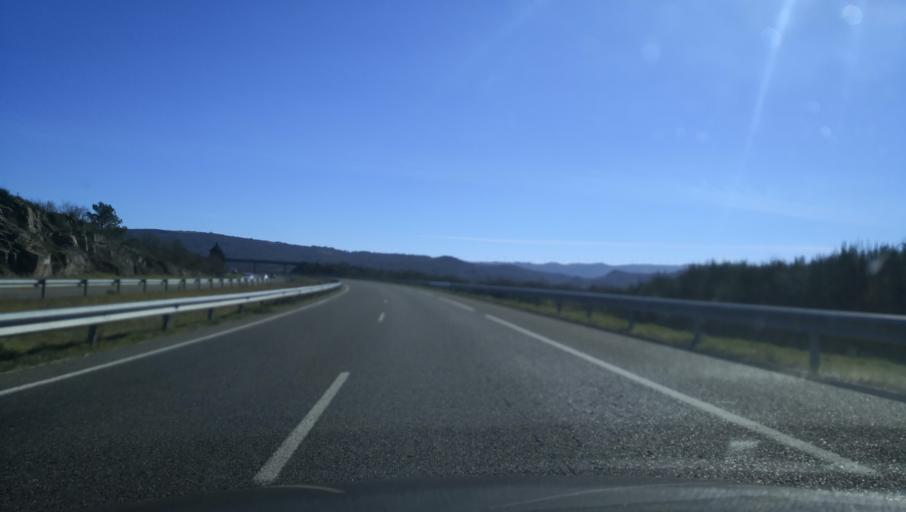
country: ES
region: Galicia
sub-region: Provincia de Ourense
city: Trasmiras
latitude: 42.0362
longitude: -7.6577
